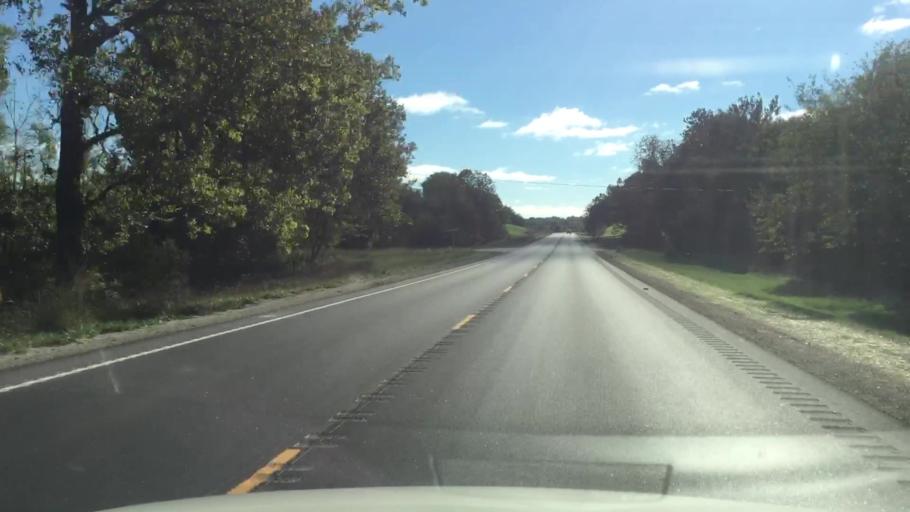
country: US
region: Missouri
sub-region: Boone County
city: Columbia
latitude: 38.9848
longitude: -92.4542
